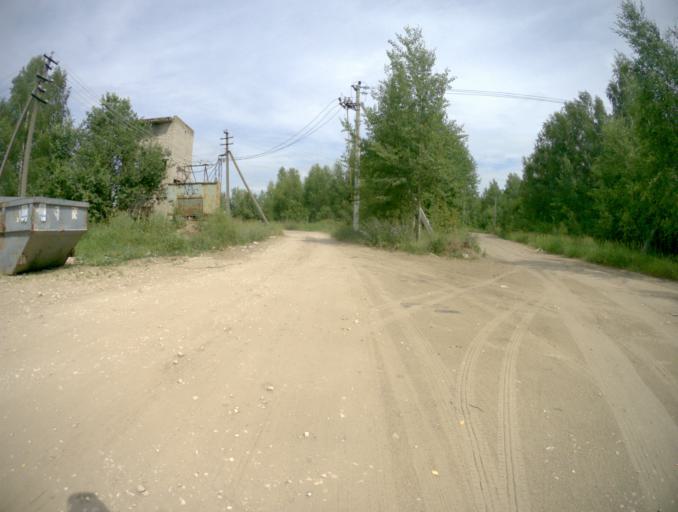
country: RU
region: Vladimir
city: Raduzhnyy
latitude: 56.0253
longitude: 40.3177
